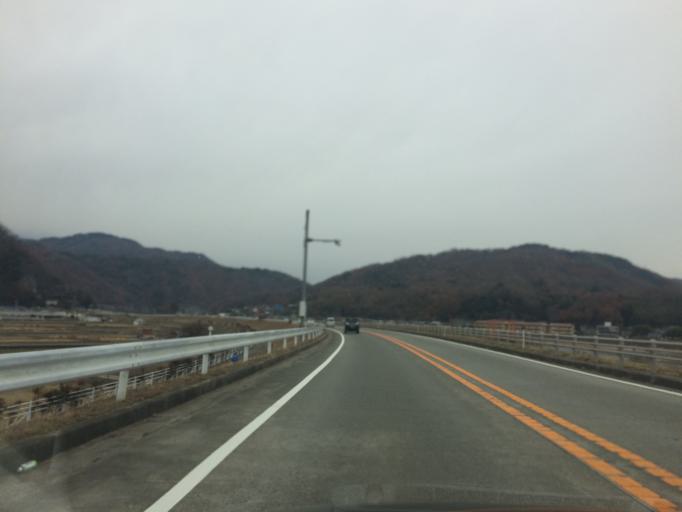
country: JP
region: Yamanashi
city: Ryuo
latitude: 35.4881
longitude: 138.4536
